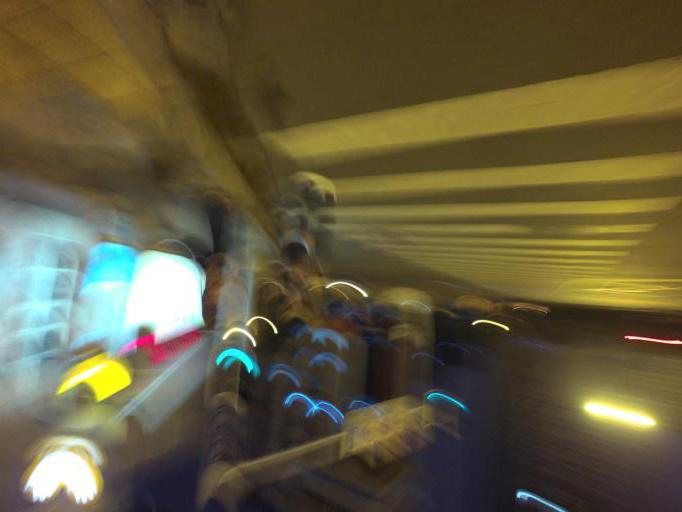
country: CN
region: Sichuan
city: Chengdu
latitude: 30.6694
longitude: 104.0580
